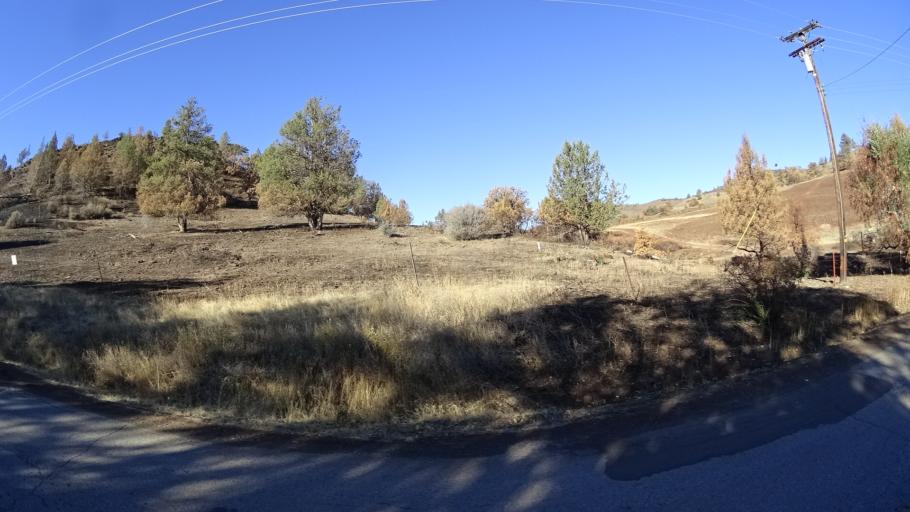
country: US
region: California
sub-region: Siskiyou County
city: Montague
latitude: 41.9118
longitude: -122.4628
